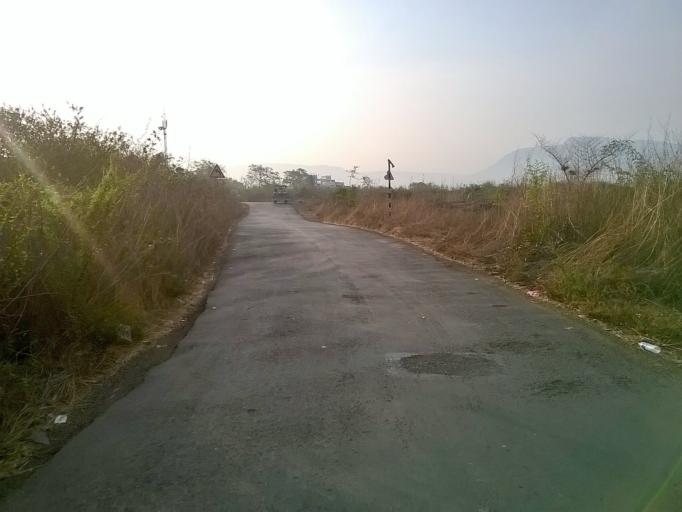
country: IN
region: Maharashtra
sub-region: Raigarh
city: Kalundri
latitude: 19.0194
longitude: 73.1843
